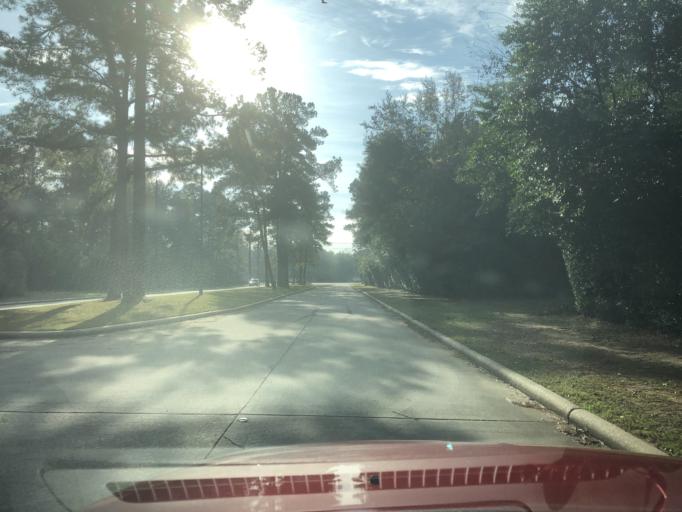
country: US
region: Texas
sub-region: Harris County
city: Spring
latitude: 30.0023
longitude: -95.4763
